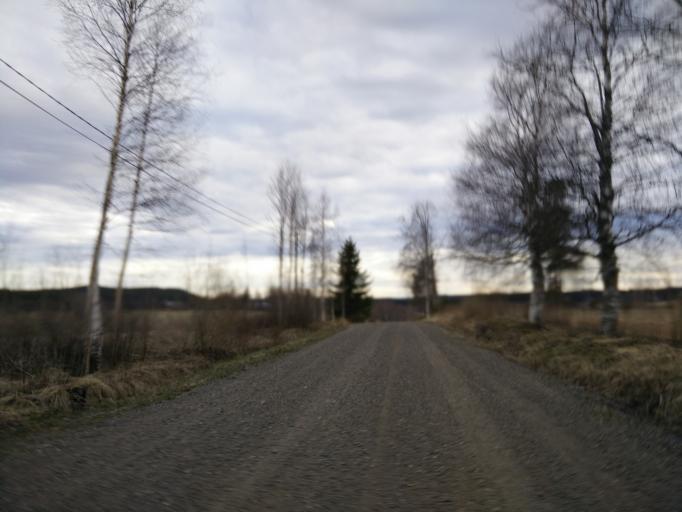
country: FI
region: Pirkanmaa
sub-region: Tampere
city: Orivesi
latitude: 61.7083
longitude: 24.3205
